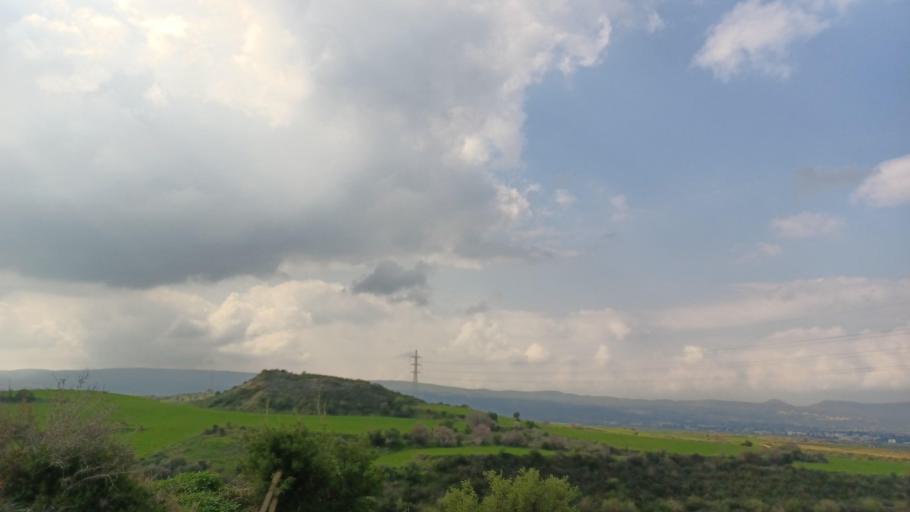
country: CY
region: Pafos
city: Polis
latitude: 35.0394
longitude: 32.4630
